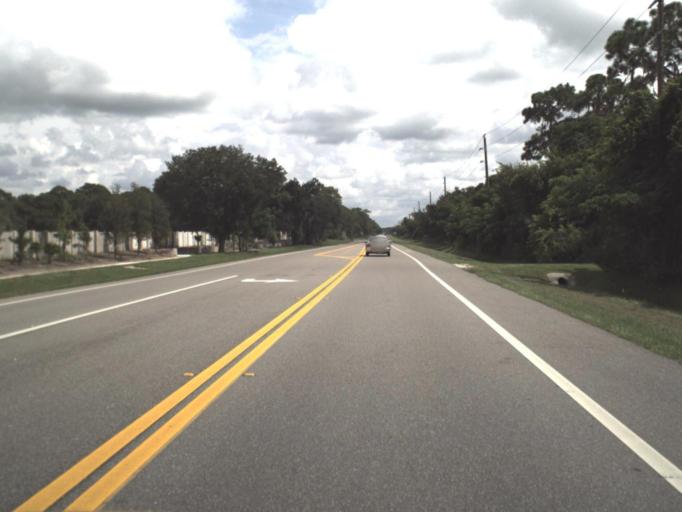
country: US
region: Florida
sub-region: Sarasota County
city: Lake Sarasota
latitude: 27.2624
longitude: -82.4086
